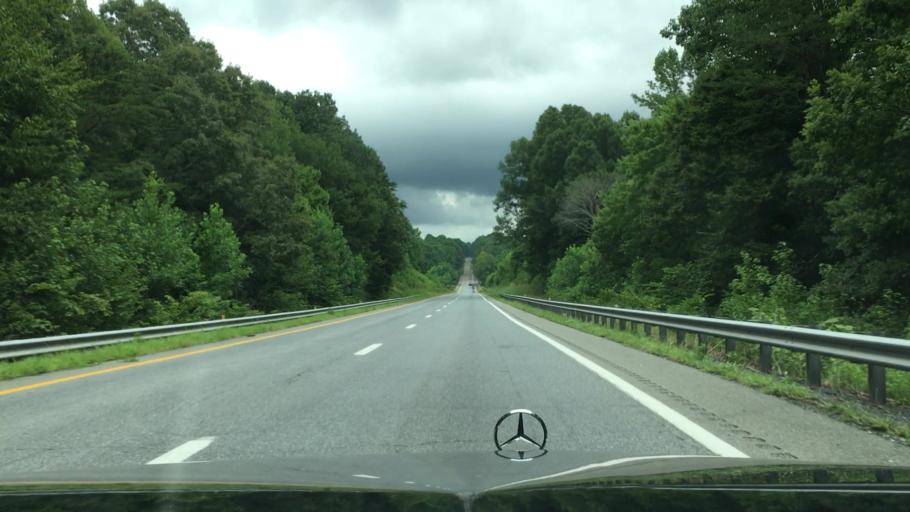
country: US
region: Virginia
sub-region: Appomattox County
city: Appomattox
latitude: 37.2723
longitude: -78.6764
